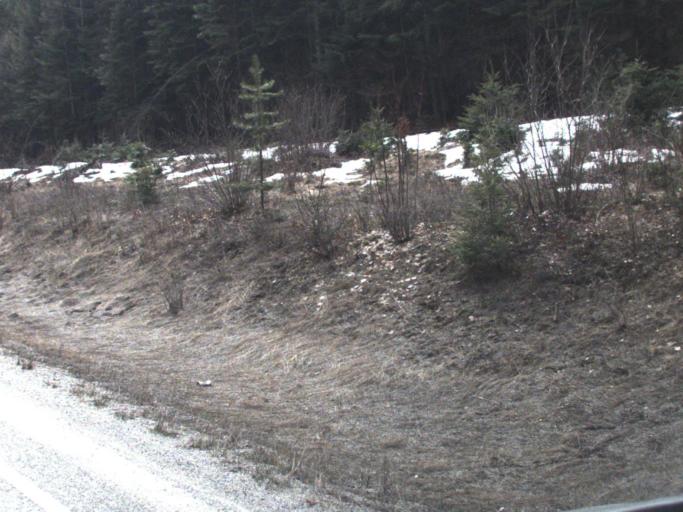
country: US
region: Washington
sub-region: Pend Oreille County
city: Newport
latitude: 48.5154
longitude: -117.2834
